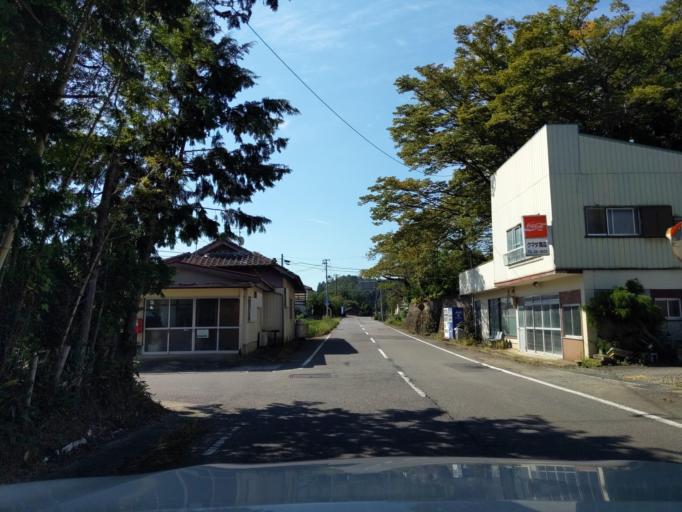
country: JP
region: Fukushima
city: Koriyama
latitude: 37.3759
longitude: 140.2621
